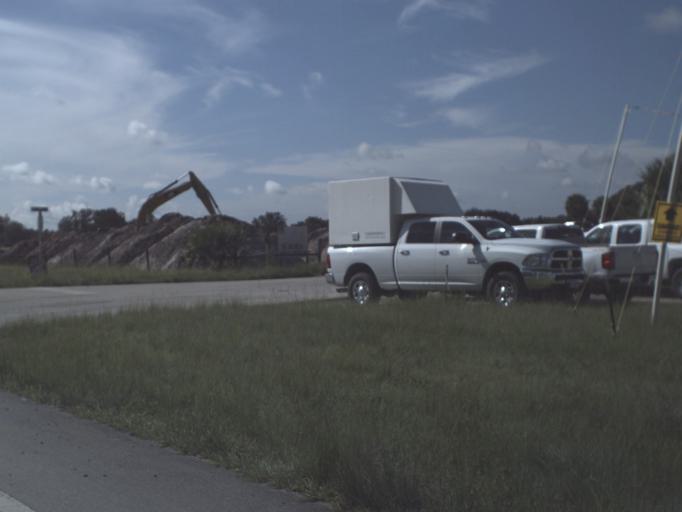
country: US
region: Florida
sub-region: Indian River County
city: Fellsmere
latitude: 27.5625
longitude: -80.8264
